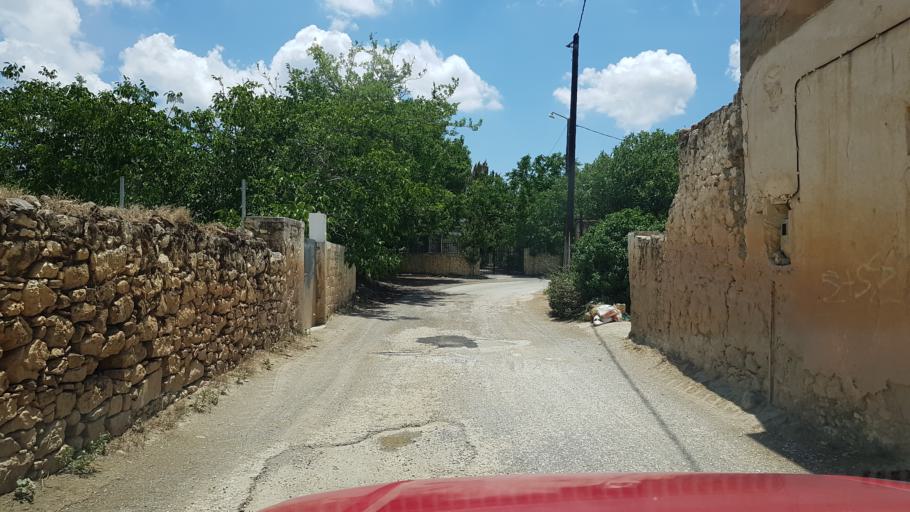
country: GR
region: Crete
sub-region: Nomos Irakleiou
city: Agioi Deka
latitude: 35.0125
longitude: 24.9997
